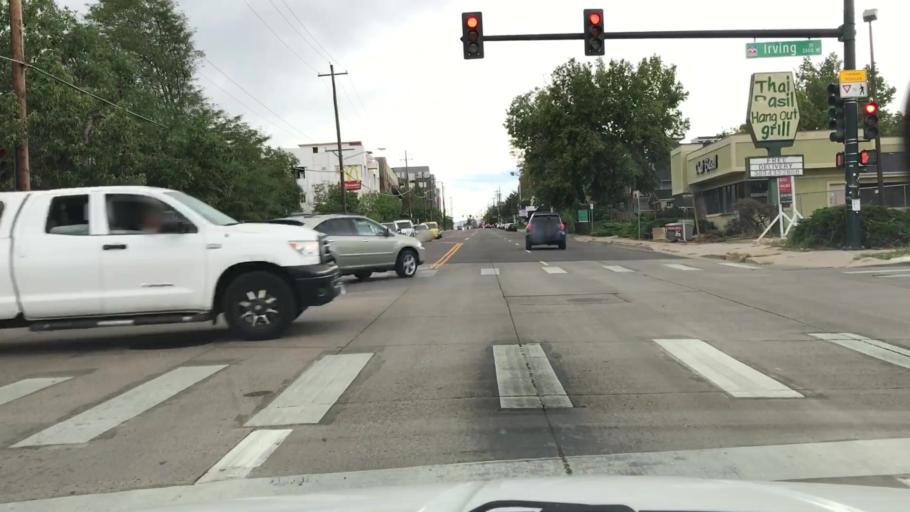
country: US
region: Colorado
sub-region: Adams County
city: Berkley
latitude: 39.7694
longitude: -105.0298
